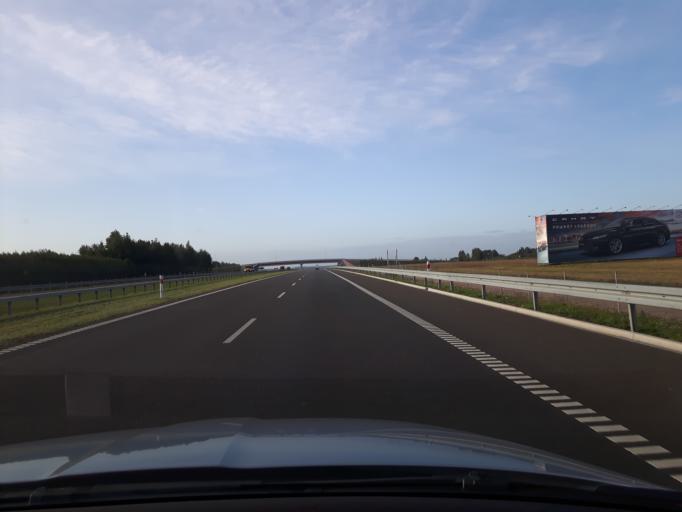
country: PL
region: Masovian Voivodeship
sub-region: Powiat radomski
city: Jedlinsk
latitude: 51.5160
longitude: 21.0841
